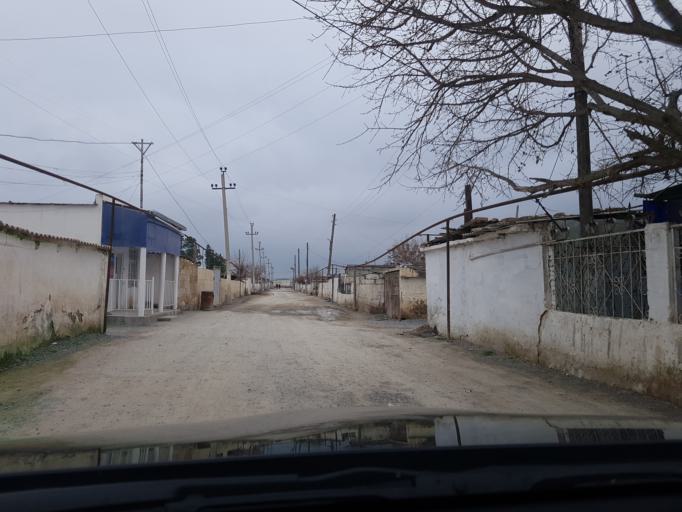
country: TM
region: Ahal
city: Abadan
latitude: 38.1582
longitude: 57.9544
